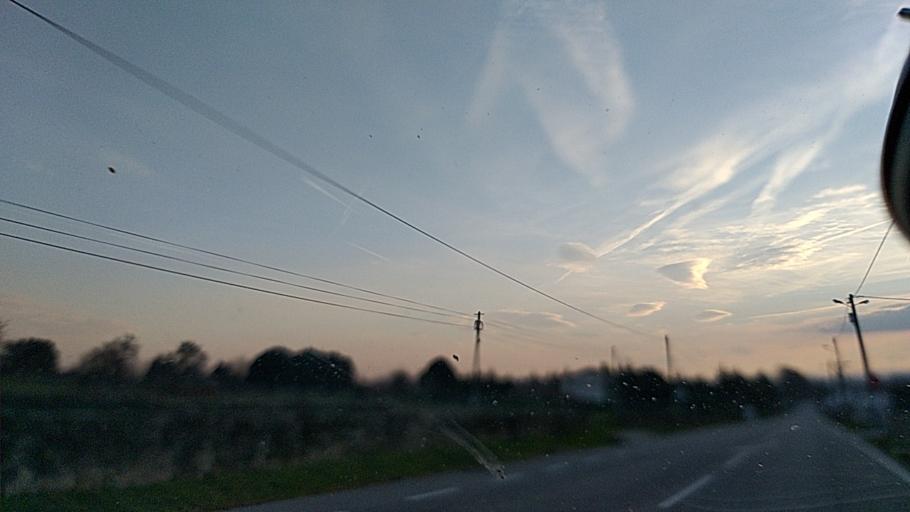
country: PT
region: Guarda
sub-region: Guarda
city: Sequeira
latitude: 40.5924
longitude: -7.1388
